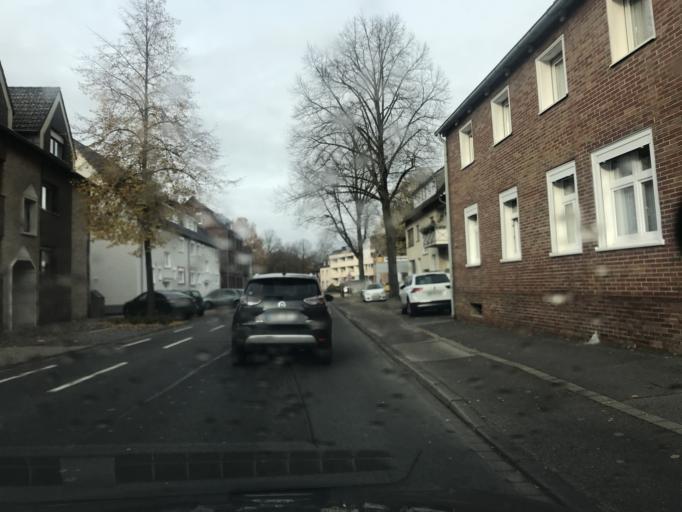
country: DE
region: North Rhine-Westphalia
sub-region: Regierungsbezirk Arnsberg
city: Hamm
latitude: 51.6835
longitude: 7.8523
